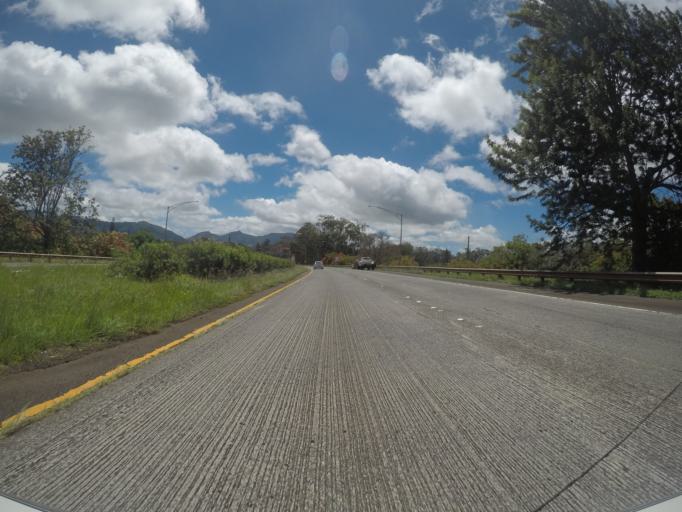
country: US
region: Hawaii
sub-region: Honolulu County
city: Wahiawa
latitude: 21.4902
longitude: -158.0292
